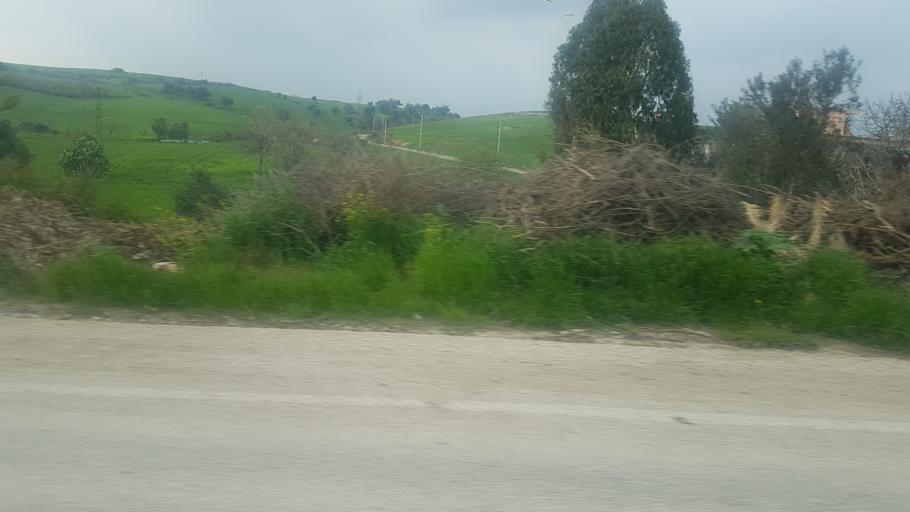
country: TR
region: Adana
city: Seyhan
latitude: 37.0574
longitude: 35.2258
